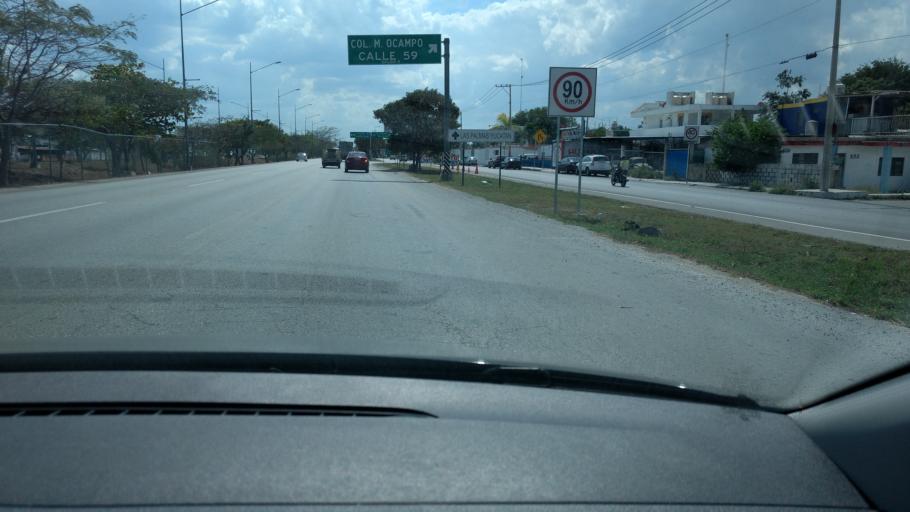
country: MX
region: Yucatan
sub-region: Kanasin
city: Kanasin
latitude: 20.9737
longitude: -89.5652
